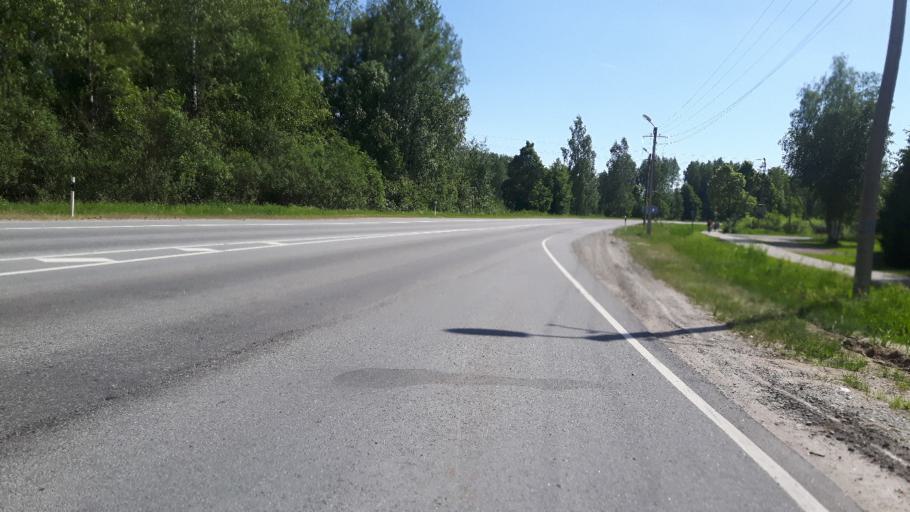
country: EE
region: Paernumaa
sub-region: Paikuse vald
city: Paikuse
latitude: 58.3866
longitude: 24.6396
